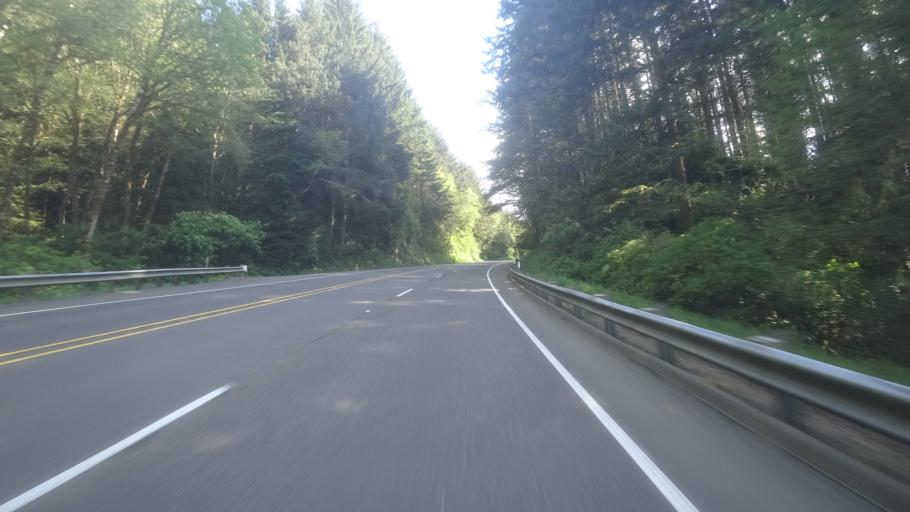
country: US
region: Oregon
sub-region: Douglas County
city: Reedsport
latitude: 43.7823
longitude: -124.1420
